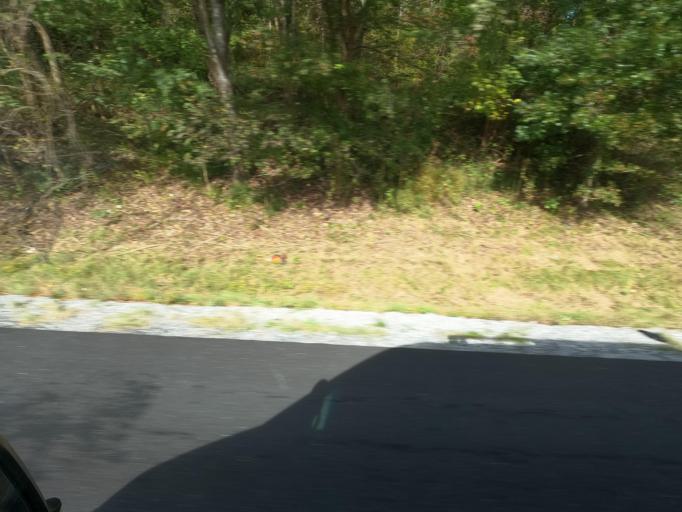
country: US
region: Tennessee
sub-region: Humphreys County
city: McEwen
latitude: 35.9282
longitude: -87.5863
